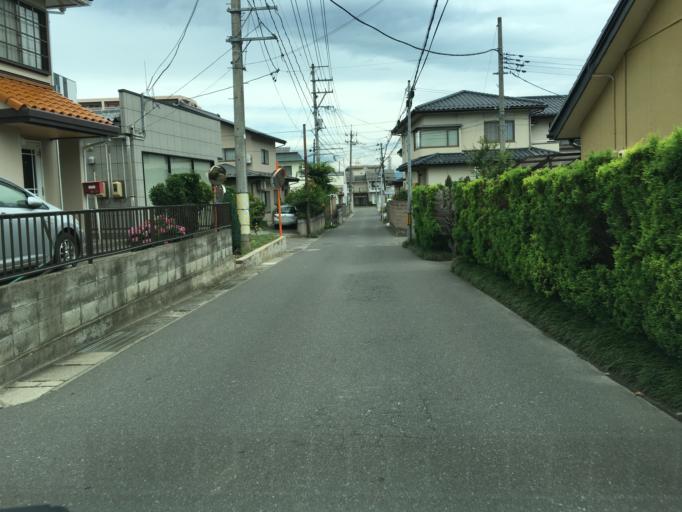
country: JP
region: Fukushima
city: Fukushima-shi
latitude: 37.7284
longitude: 140.4415
